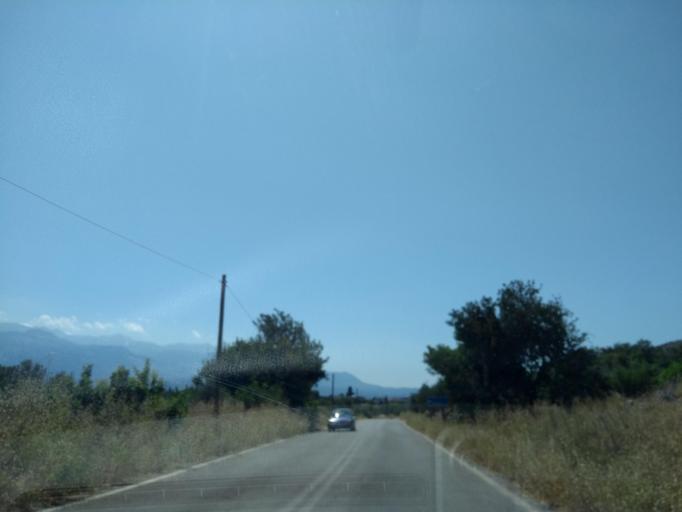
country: GR
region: Crete
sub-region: Nomos Chanias
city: Georgioupolis
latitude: 35.3817
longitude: 24.2391
